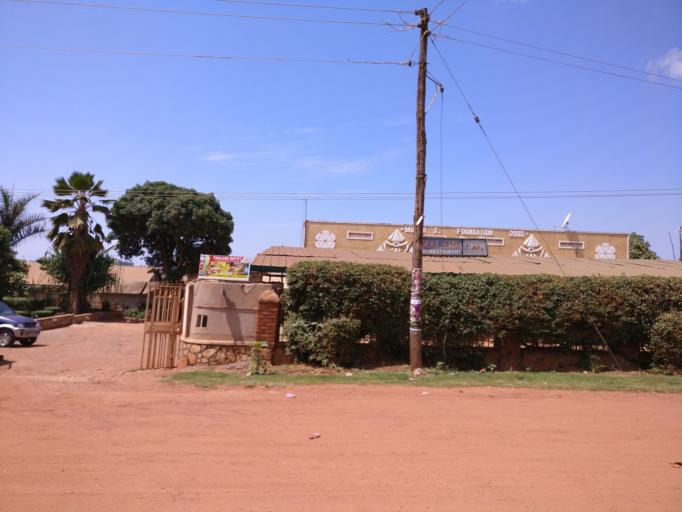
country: UG
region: Central Region
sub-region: Wakiso District
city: Kajansi
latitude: 0.1392
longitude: 32.5397
